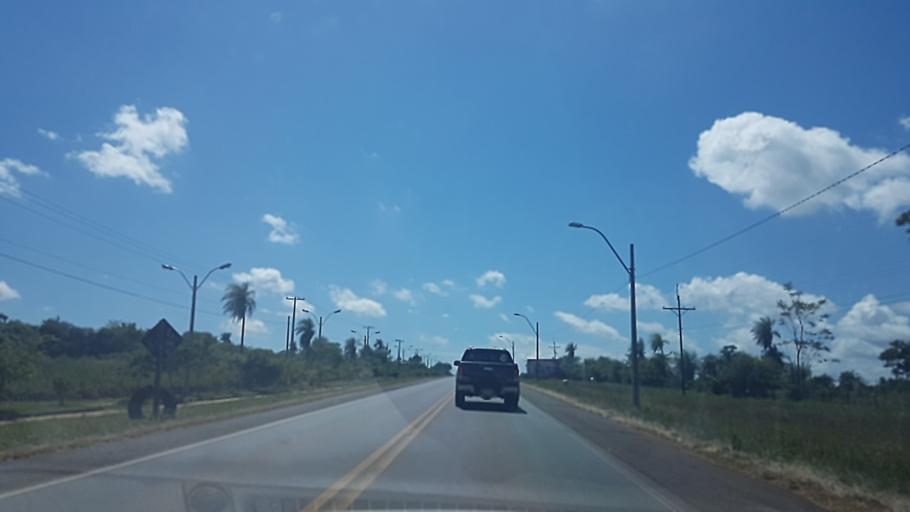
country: PY
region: Misiones
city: San Juan Bautista
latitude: -26.6724
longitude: -57.1246
